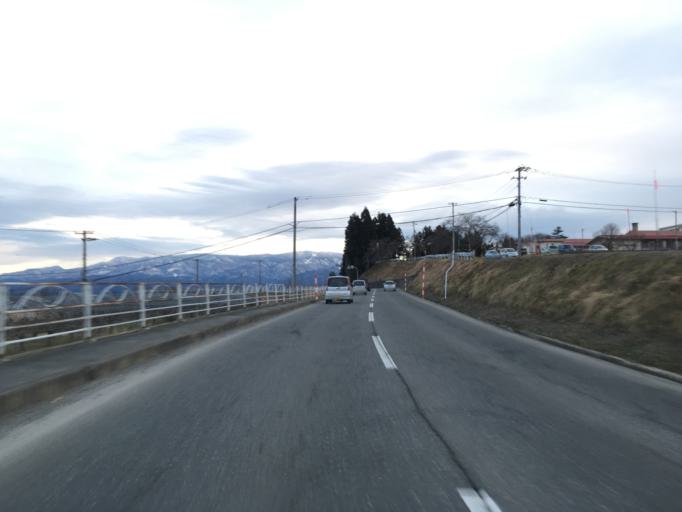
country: JP
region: Yamagata
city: Yonezawa
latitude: 37.9364
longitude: 140.0781
